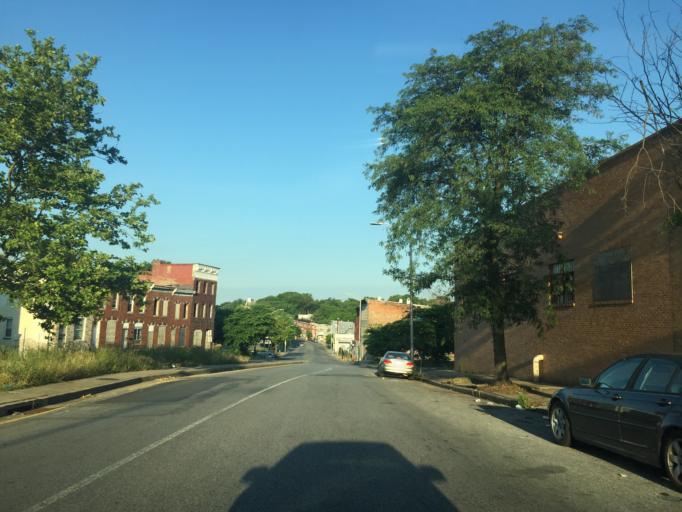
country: US
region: Maryland
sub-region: City of Baltimore
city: Baltimore
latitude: 39.2852
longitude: -76.6517
